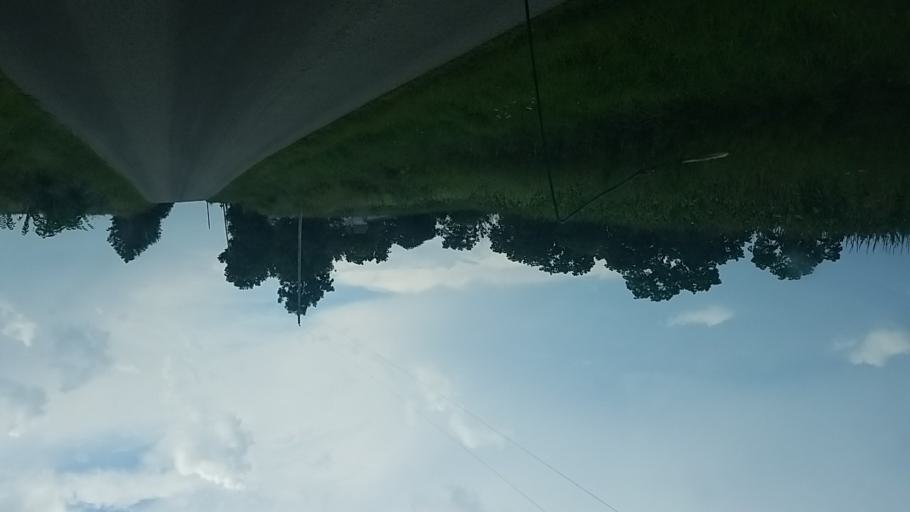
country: US
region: Ohio
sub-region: Wayne County
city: Creston
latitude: 40.9815
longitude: -81.9386
